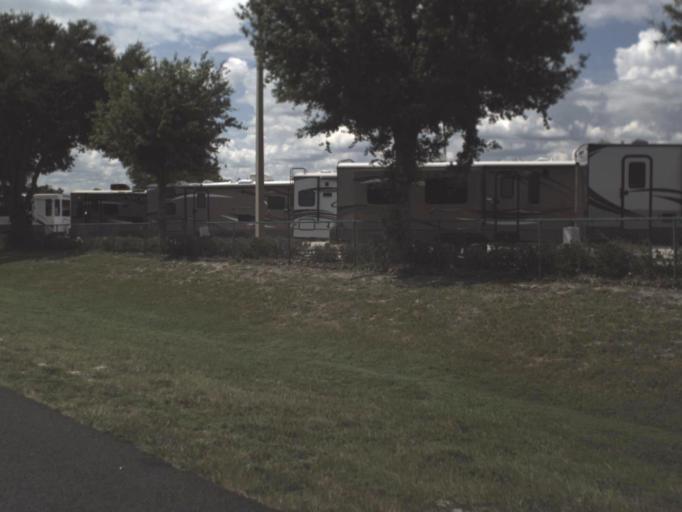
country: US
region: Florida
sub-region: Polk County
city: Wahneta
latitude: 27.9165
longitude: -81.7297
